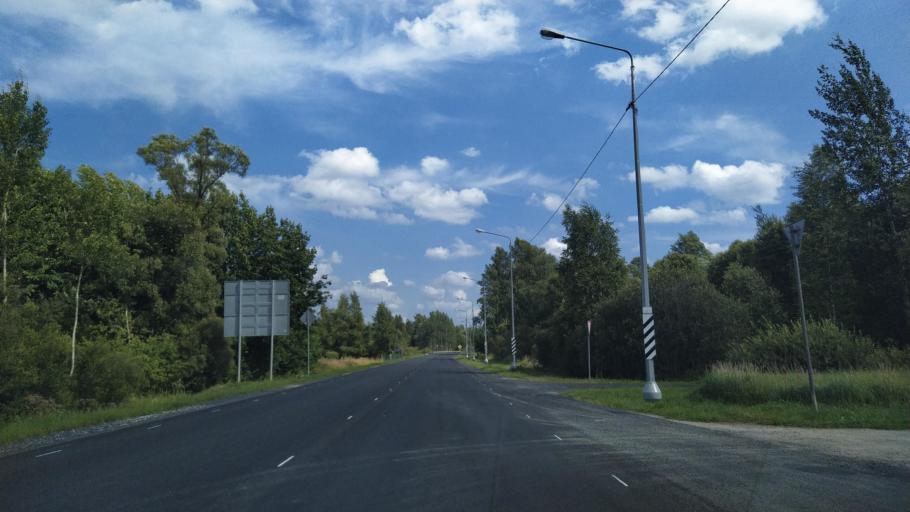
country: RU
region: Pskov
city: Porkhov
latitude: 57.7276
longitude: 29.1601
